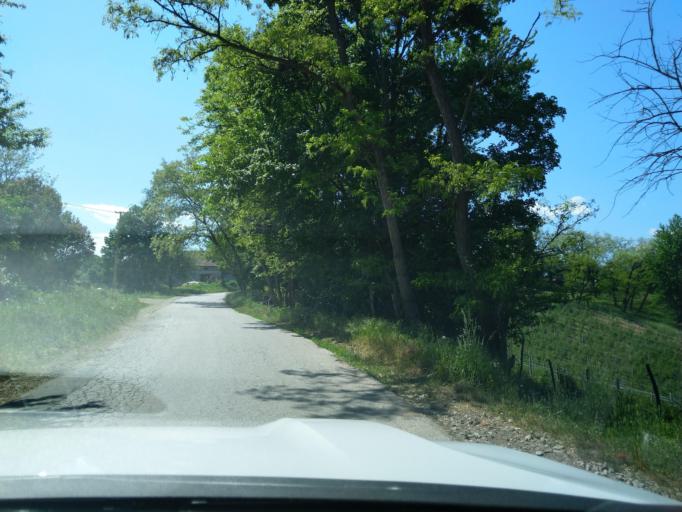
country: RS
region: Central Serbia
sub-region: Zlatiborski Okrug
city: Pozega
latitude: 43.8639
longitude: 19.9439
